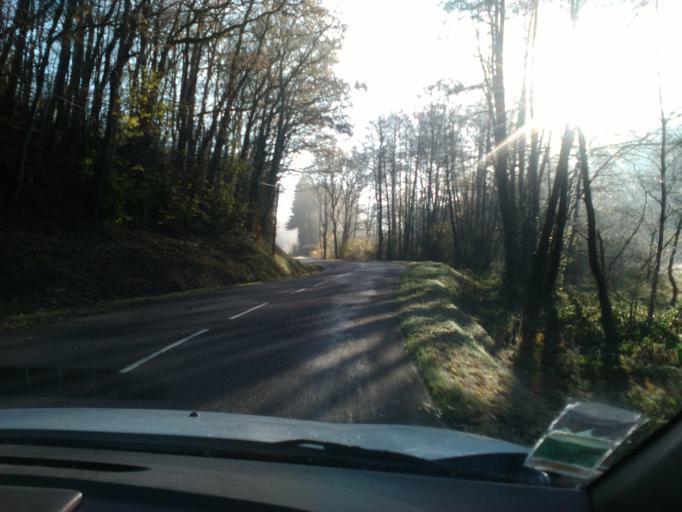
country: FR
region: Lorraine
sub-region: Departement des Vosges
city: Uzemain
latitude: 48.0603
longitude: 6.3393
